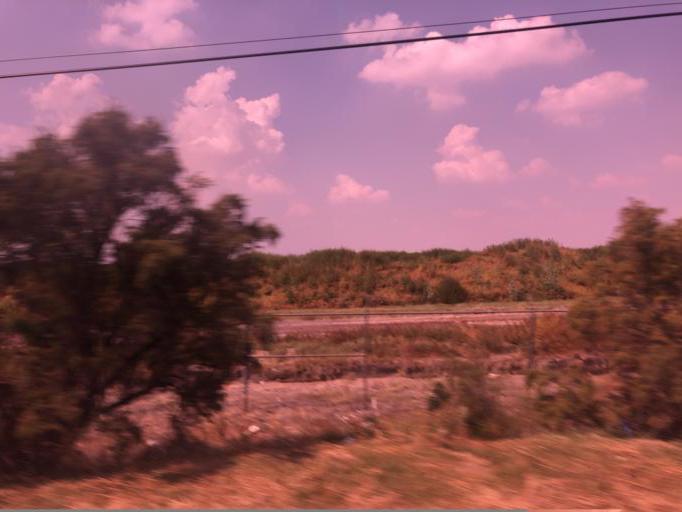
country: MX
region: Mexico
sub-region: Ciudad Nezahualcoyotl
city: Colonia Gustavo Baz Prada
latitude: 19.4649
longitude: -99.0174
